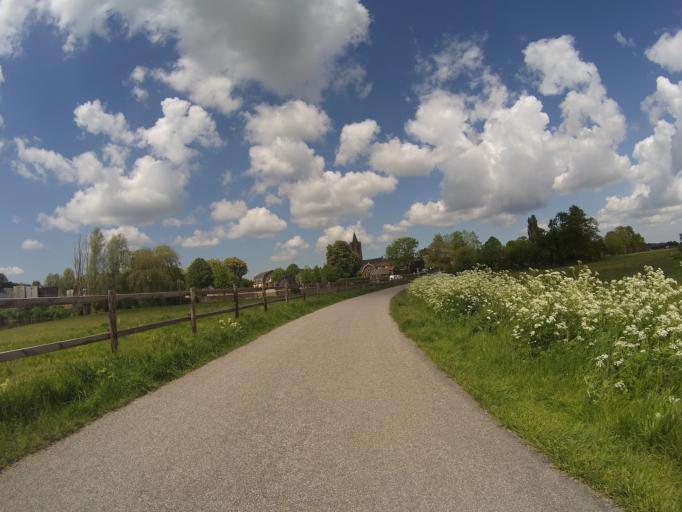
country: NL
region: North Holland
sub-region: Gemeente Blaricum
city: Blaricum
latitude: 52.2501
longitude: 5.2681
